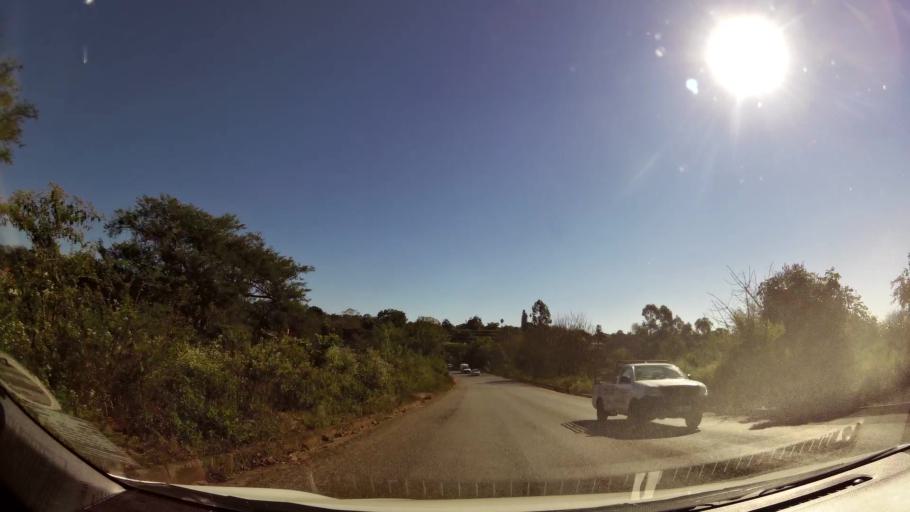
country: ZA
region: Limpopo
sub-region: Mopani District Municipality
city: Tzaneen
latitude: -23.8402
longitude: 30.1668
